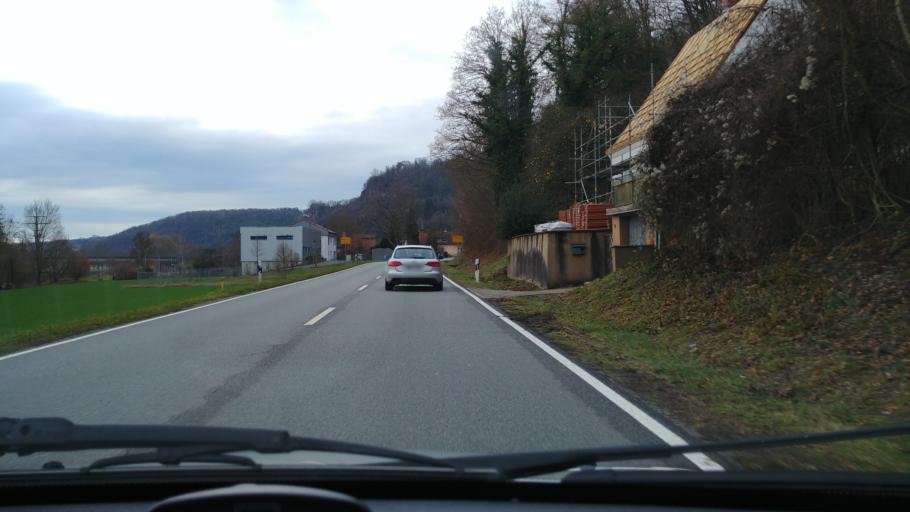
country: DE
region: Bavaria
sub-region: Regierungsbezirk Unterfranken
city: Karlstadt
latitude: 49.9627
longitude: 9.7592
